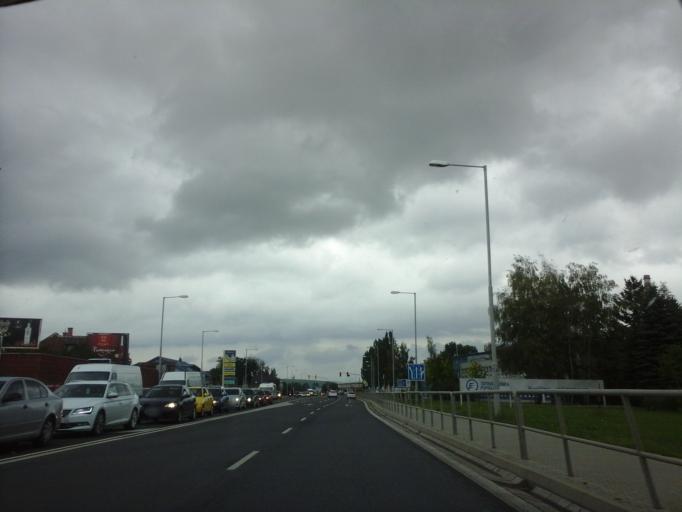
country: SK
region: Presovsky
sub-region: Okres Poprad
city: Poprad
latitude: 49.0604
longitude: 20.3123
